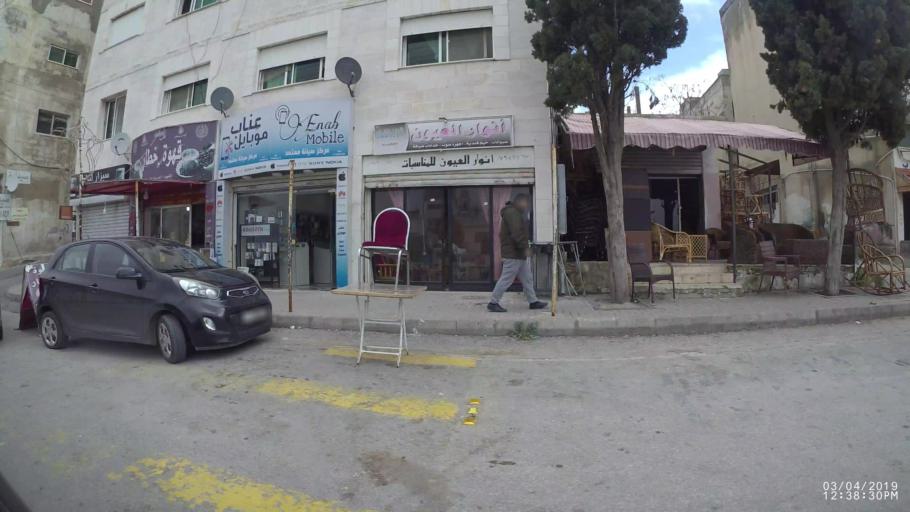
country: JO
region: Amman
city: Wadi as Sir
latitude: 31.9561
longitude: 35.8349
